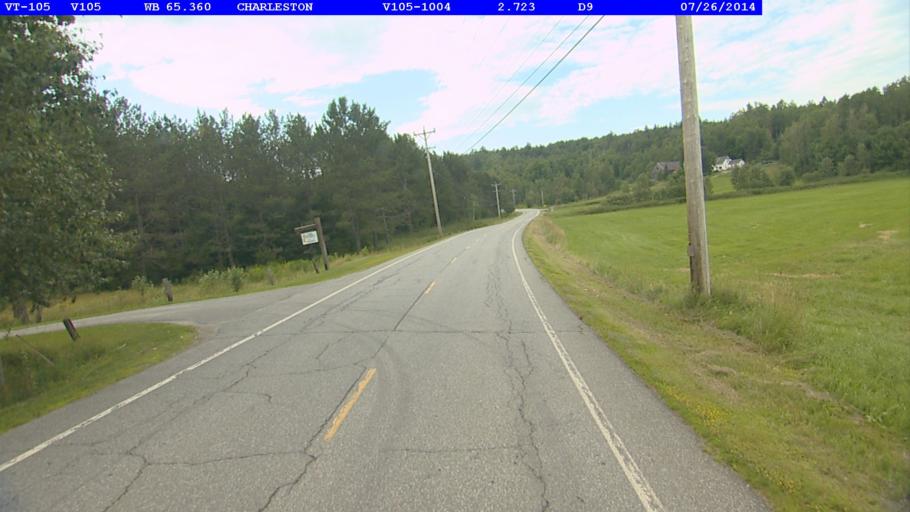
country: US
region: Vermont
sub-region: Orleans County
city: Newport
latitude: 44.8771
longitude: -72.0516
